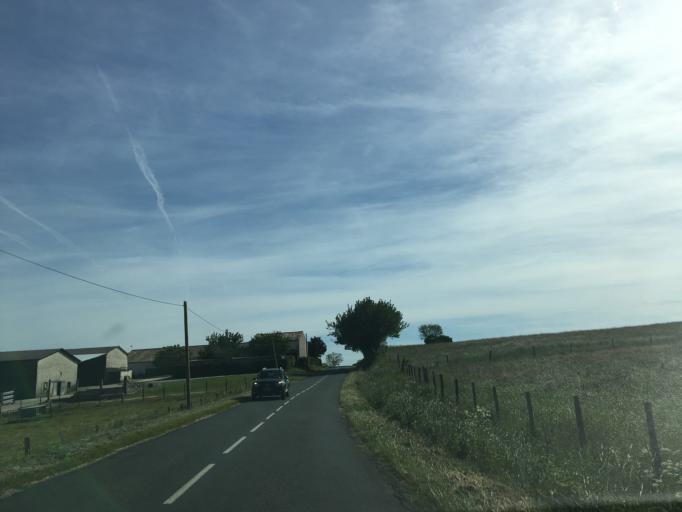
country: FR
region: Poitou-Charentes
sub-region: Departement de la Charente-Maritime
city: Mirambeau
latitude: 45.3400
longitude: -0.5885
